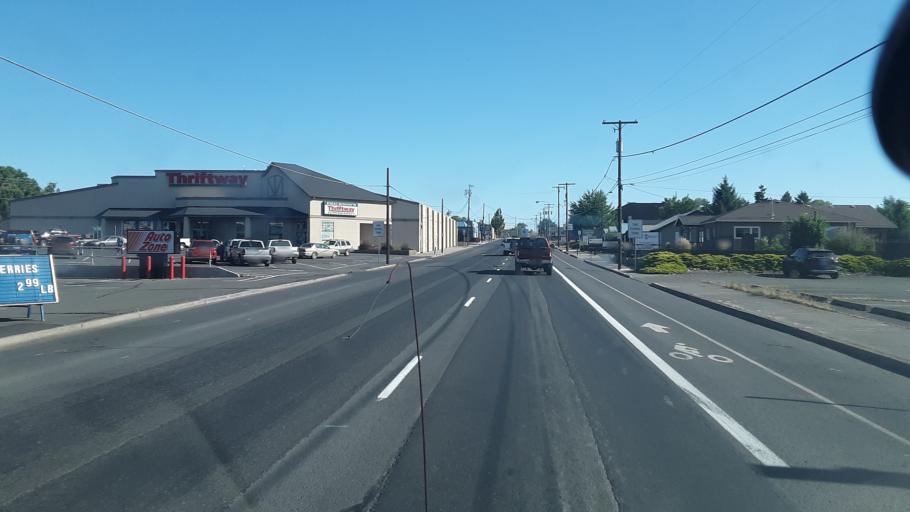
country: US
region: Oregon
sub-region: Jefferson County
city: Madras
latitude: 44.6291
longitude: -121.1306
